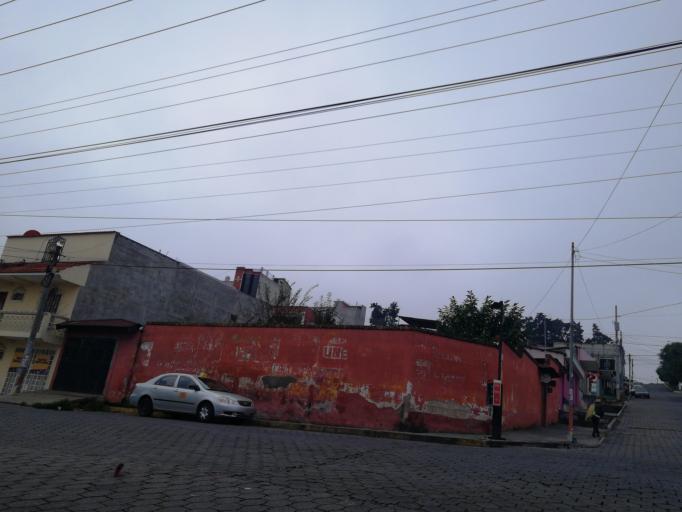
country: GT
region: Quetzaltenango
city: Quetzaltenango
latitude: 14.8501
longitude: -91.5164
